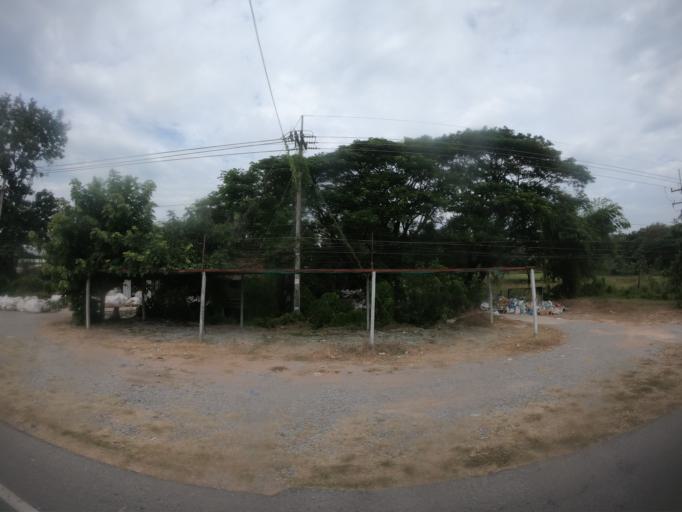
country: TH
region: Maha Sarakham
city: Maha Sarakham
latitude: 16.1472
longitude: 103.4072
